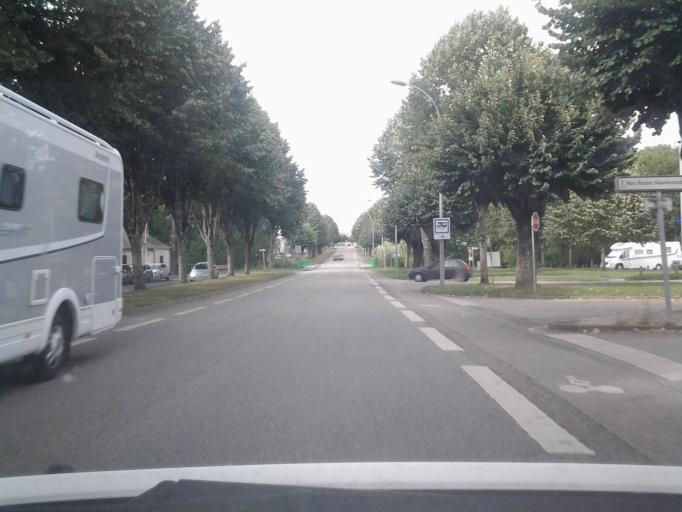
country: FR
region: Pays de la Loire
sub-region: Departement de la Vendee
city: La Roche-sur-Yon
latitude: 46.6678
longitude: -1.4193
